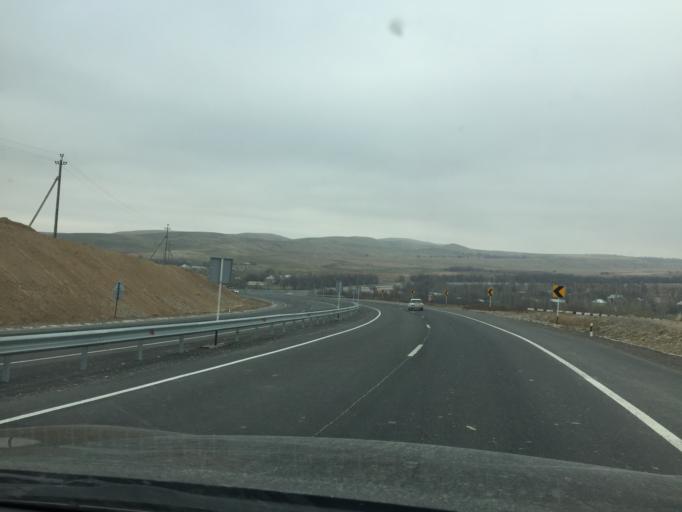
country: KZ
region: Ongtustik Qazaqstan
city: Sastobe
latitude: 42.4942
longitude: 69.9596
